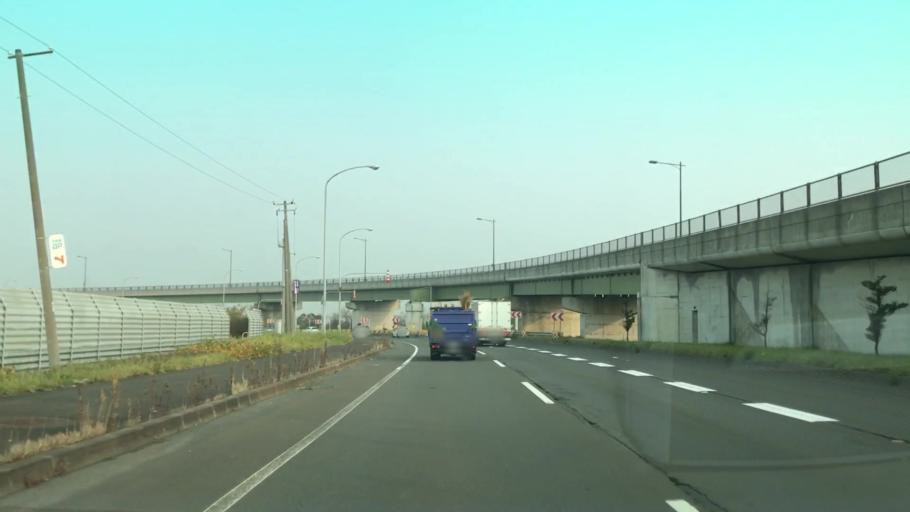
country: JP
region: Hokkaido
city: Ishikari
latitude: 43.1781
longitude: 141.3479
